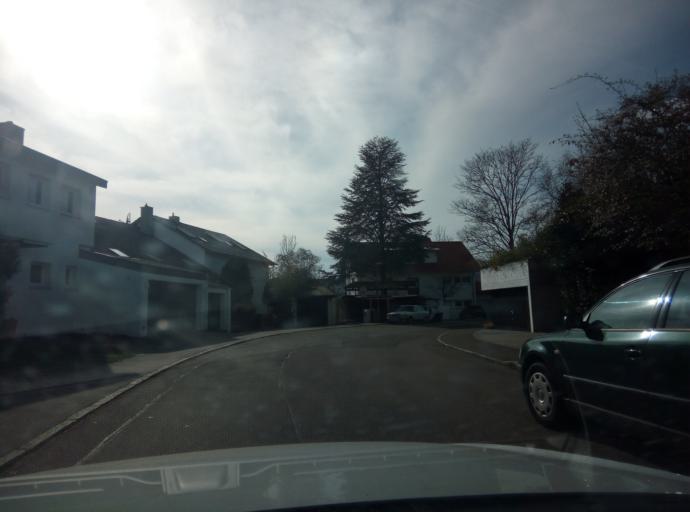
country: DE
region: Baden-Wuerttemberg
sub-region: Tuebingen Region
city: Tuebingen
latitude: 48.5320
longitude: 9.0497
